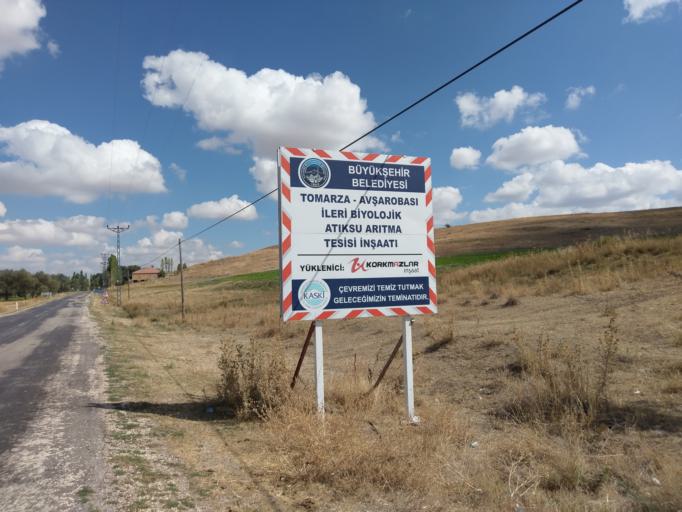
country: TR
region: Kayseri
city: Toklar
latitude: 38.4535
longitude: 36.0688
